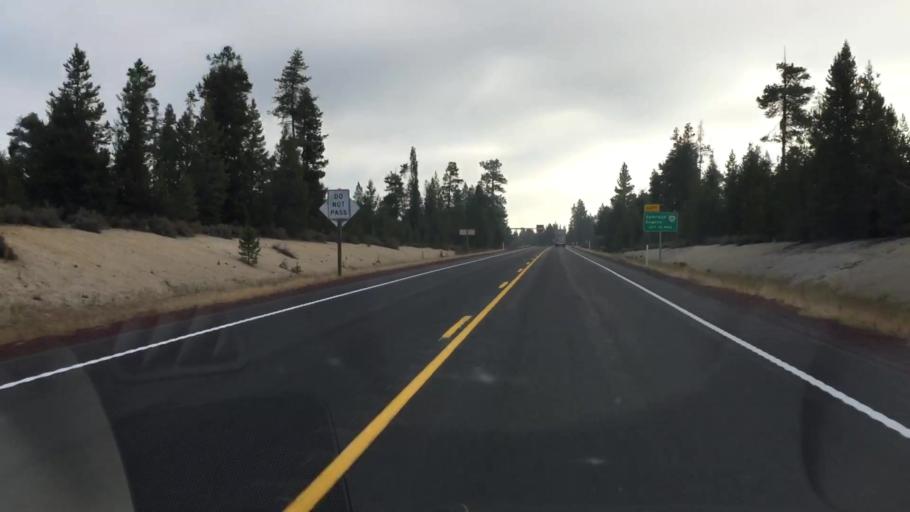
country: US
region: Oregon
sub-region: Deschutes County
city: La Pine
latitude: 43.3217
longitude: -121.7622
